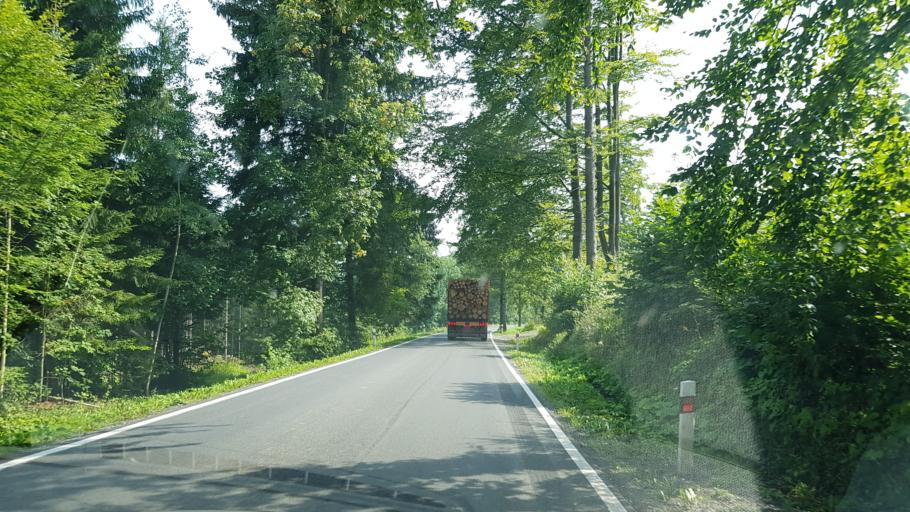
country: CZ
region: Olomoucky
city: Mikulovice
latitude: 50.2358
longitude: 17.3354
